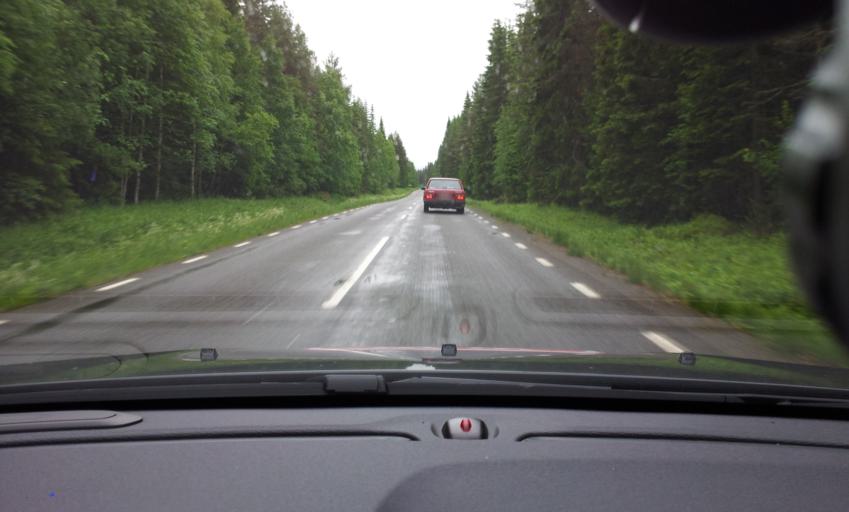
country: SE
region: Jaemtland
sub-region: Stroemsunds Kommun
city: Stroemsund
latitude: 63.4666
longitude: 15.4551
